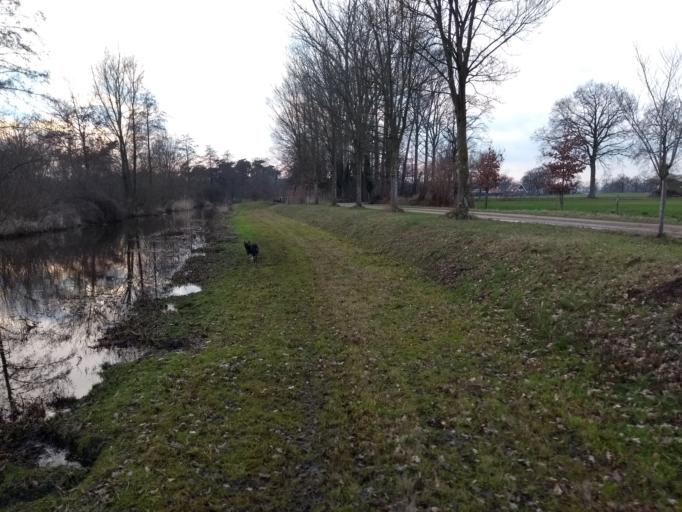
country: NL
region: Overijssel
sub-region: Gemeente Borne
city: Borne
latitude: 52.3347
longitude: 6.7433
